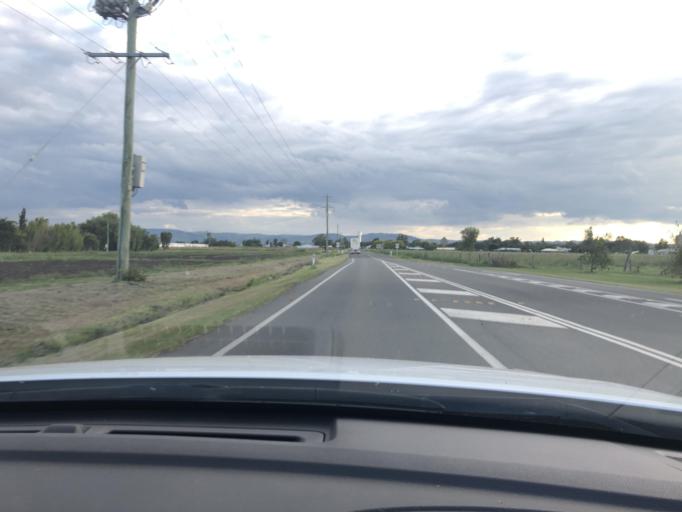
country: AU
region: Queensland
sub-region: Lockyer Valley
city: Gatton
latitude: -27.5842
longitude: 152.3634
